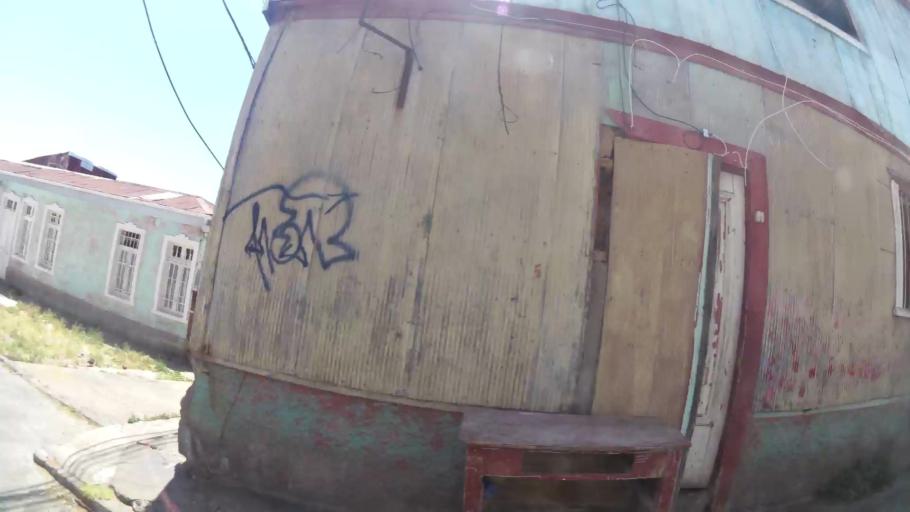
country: CL
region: Valparaiso
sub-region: Provincia de Valparaiso
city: Valparaiso
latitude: -33.0419
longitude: -71.6332
